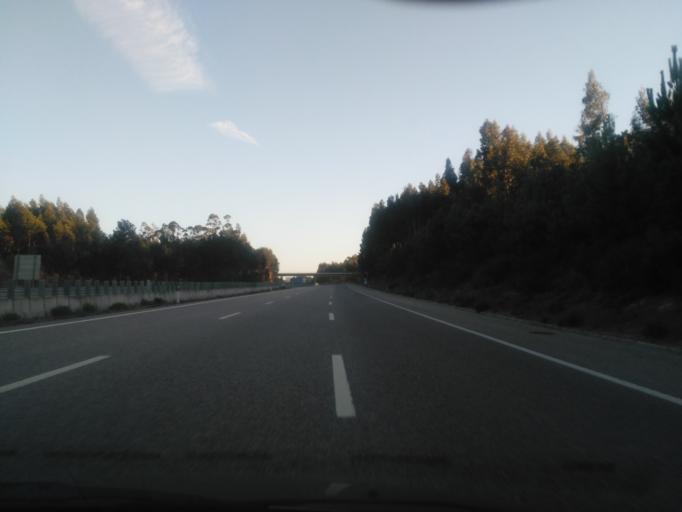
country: PT
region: Leiria
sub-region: Pombal
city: Lourical
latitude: 39.9994
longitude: -8.7984
